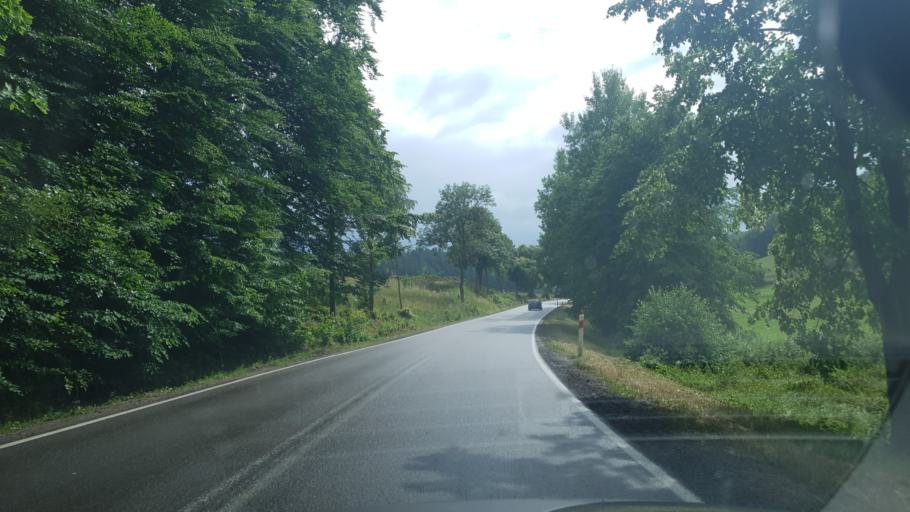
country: PL
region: Pomeranian Voivodeship
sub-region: Powiat kartuski
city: Kartuzy
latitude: 54.3148
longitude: 18.1631
